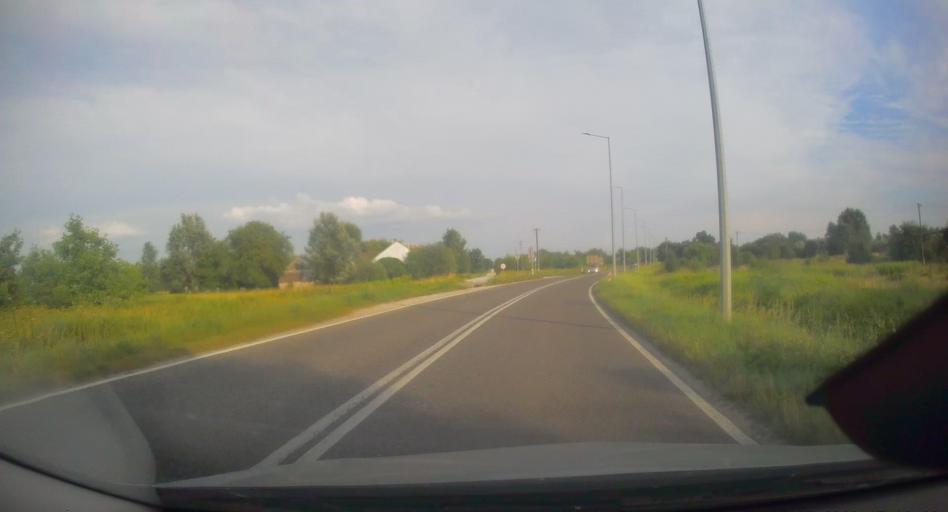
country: PL
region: Lesser Poland Voivodeship
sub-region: Powiat brzeski
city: Szczurowa
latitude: 50.1596
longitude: 20.6025
